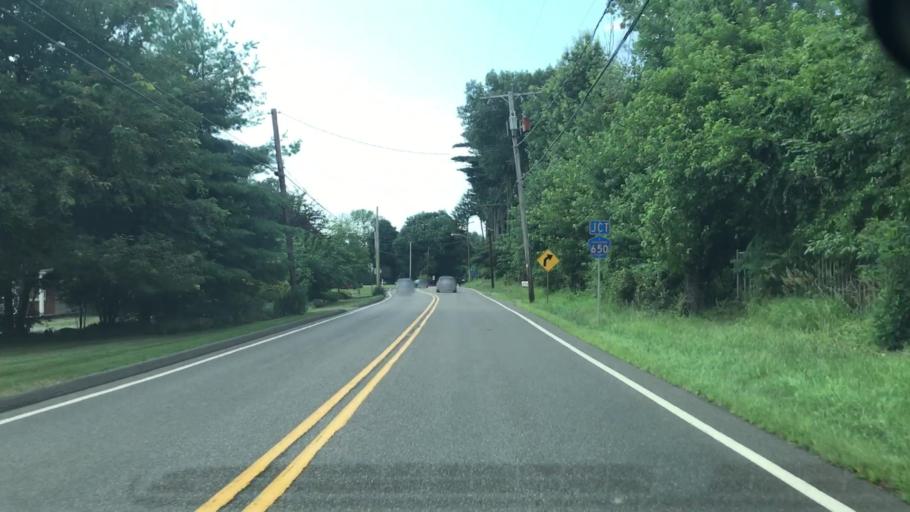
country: US
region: New Jersey
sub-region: Hunterdon County
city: Flemington
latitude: 40.5016
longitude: -74.8082
